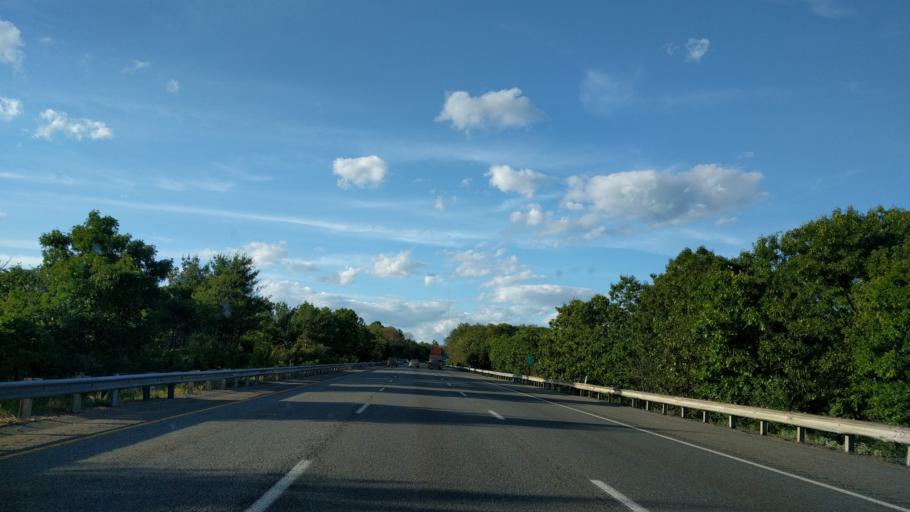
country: US
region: Massachusetts
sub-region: Worcester County
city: Shrewsbury
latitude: 42.3086
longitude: -71.7320
